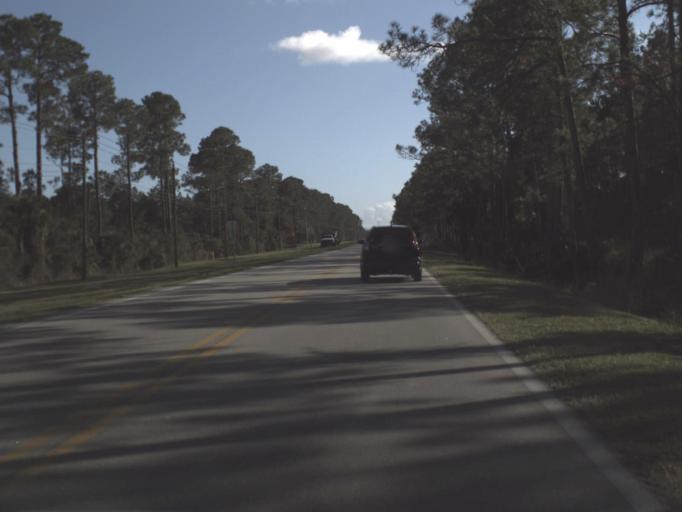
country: US
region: Florida
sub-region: Volusia County
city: Holly Hill
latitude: 29.2394
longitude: -81.0991
